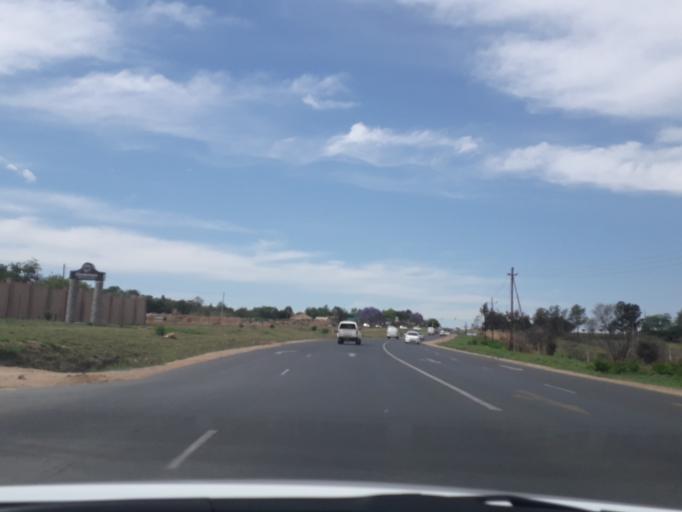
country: ZA
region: Gauteng
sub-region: City of Johannesburg Metropolitan Municipality
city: Diepsloot
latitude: -26.0041
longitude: 28.0404
